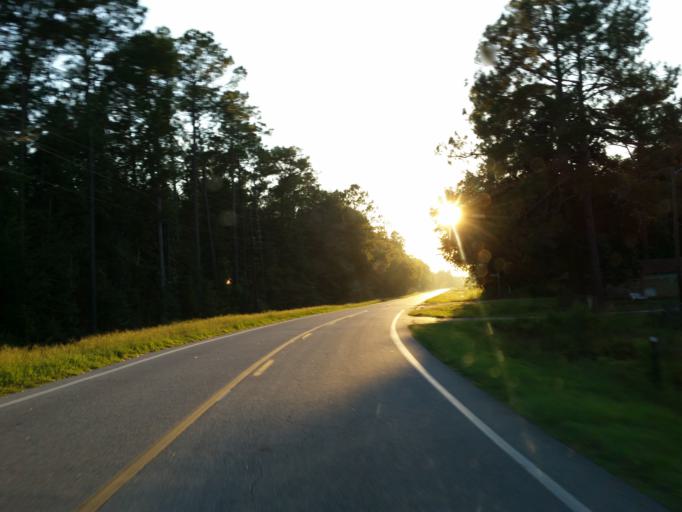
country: US
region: Georgia
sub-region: Berrien County
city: Nashville
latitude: 31.1856
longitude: -83.1888
